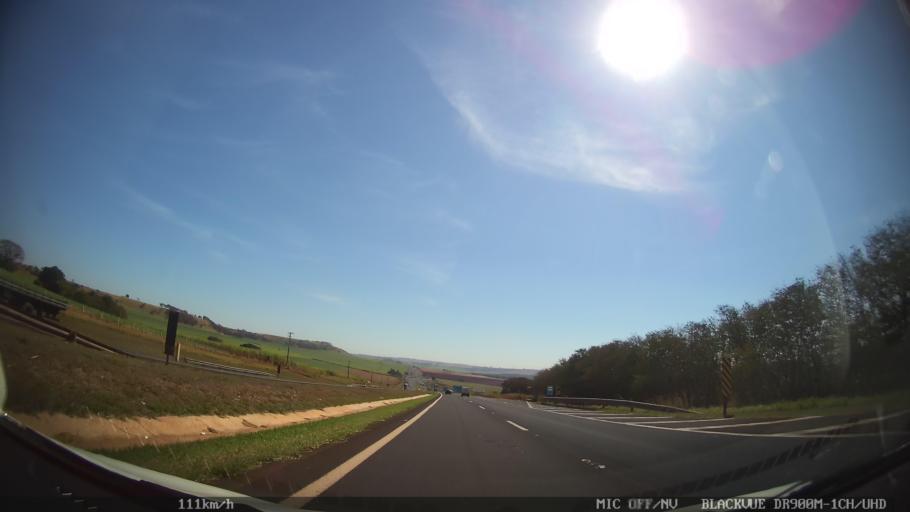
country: BR
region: Sao Paulo
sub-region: Cravinhos
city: Cravinhos
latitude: -21.4248
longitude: -47.6562
